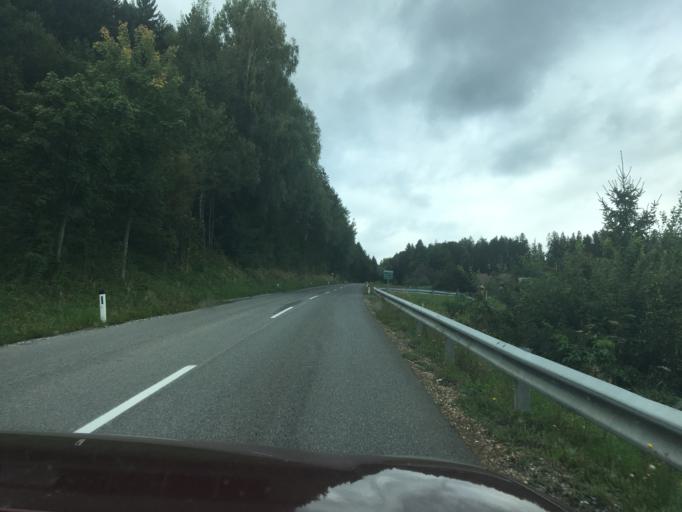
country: AT
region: Styria
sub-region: Politischer Bezirk Deutschlandsberg
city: Trahutten
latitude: 46.8064
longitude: 15.1747
